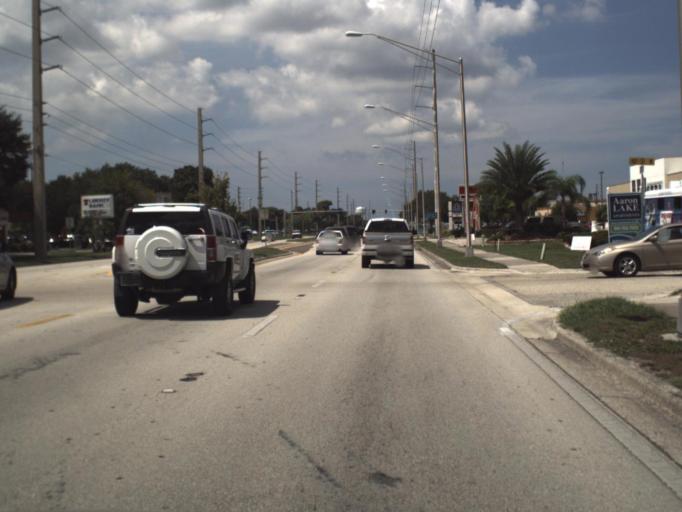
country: US
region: Florida
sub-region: Manatee County
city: South Bradenton
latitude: 27.4626
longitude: -82.6013
